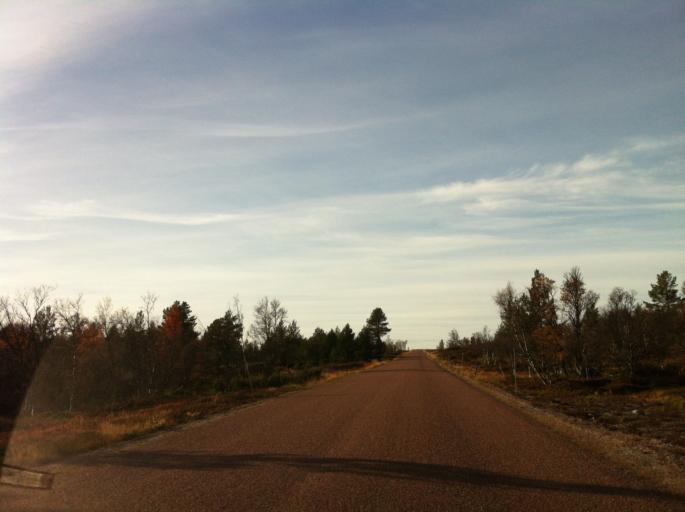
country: NO
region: Hedmark
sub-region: Engerdal
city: Engerdal
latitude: 62.0793
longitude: 12.1621
